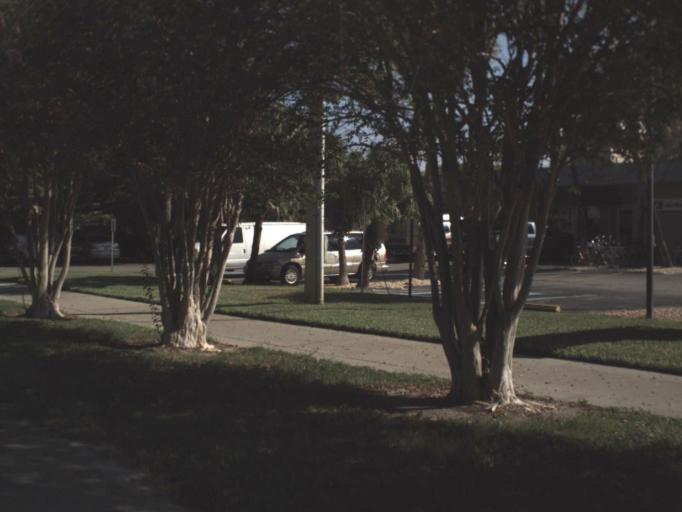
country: US
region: Florida
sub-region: Manatee County
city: Longboat Key
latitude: 27.3875
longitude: -82.6404
